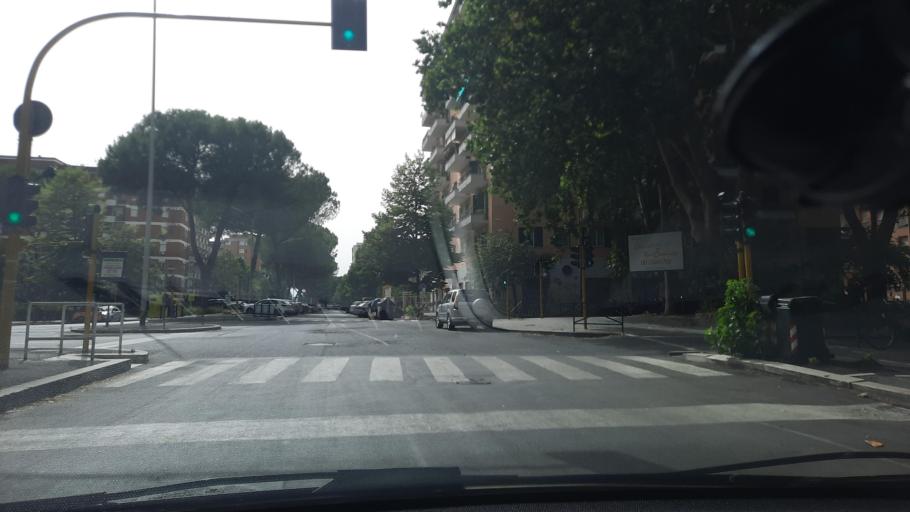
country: IT
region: Latium
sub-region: Citta metropolitana di Roma Capitale
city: Rome
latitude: 41.8560
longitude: 12.4848
